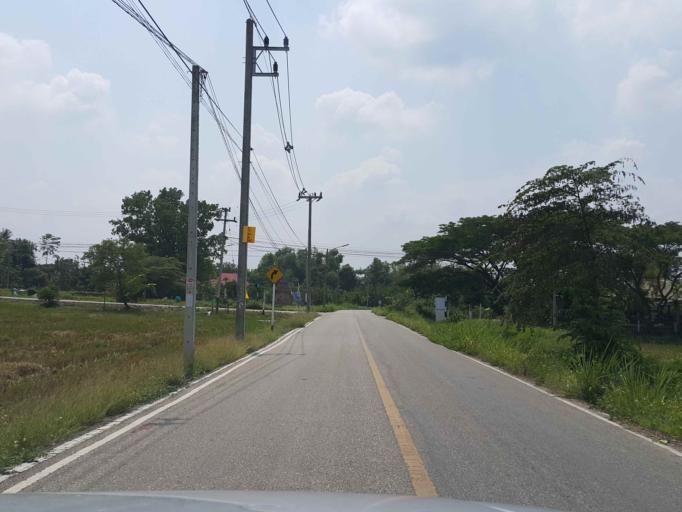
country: TH
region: Chiang Mai
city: Hang Dong
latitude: 18.7024
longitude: 98.9661
